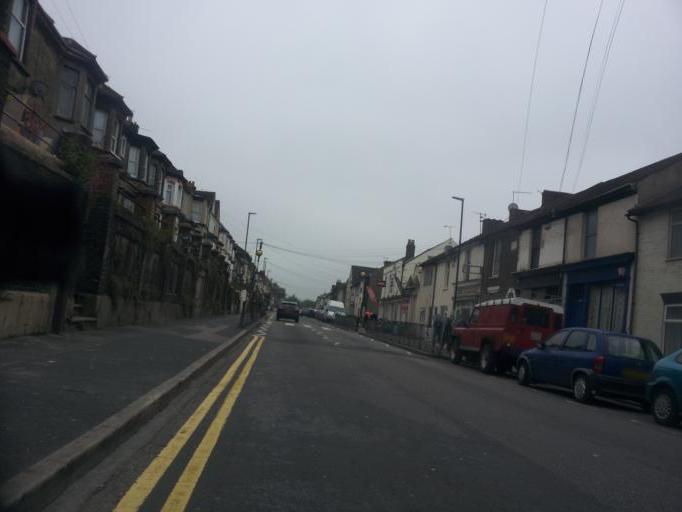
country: GB
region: England
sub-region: Kent
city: Chatham
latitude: 51.3771
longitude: 0.5359
